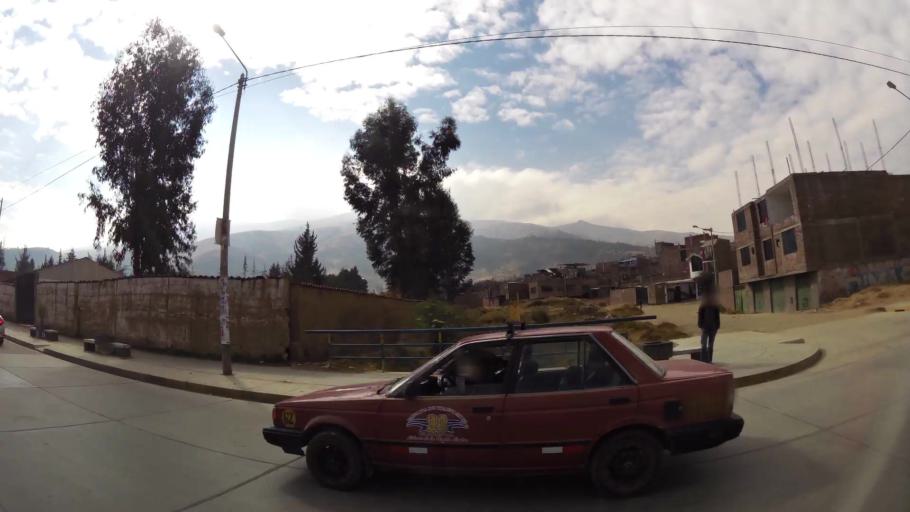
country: PE
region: Junin
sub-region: Provincia de Huancayo
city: Huancayo
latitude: -12.0556
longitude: -75.1968
